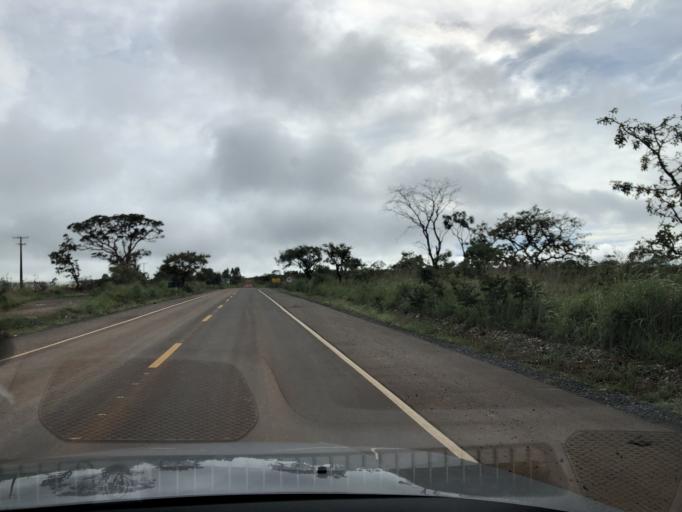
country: BR
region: Federal District
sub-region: Brasilia
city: Brasilia
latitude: -15.6186
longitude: -48.0571
